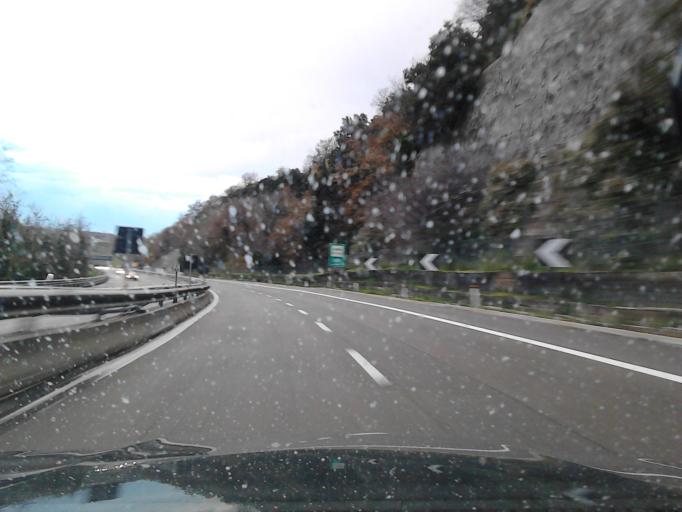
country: IT
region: Abruzzo
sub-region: Provincia di Chieti
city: San Vito Chietino
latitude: 42.2745
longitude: 14.4357
